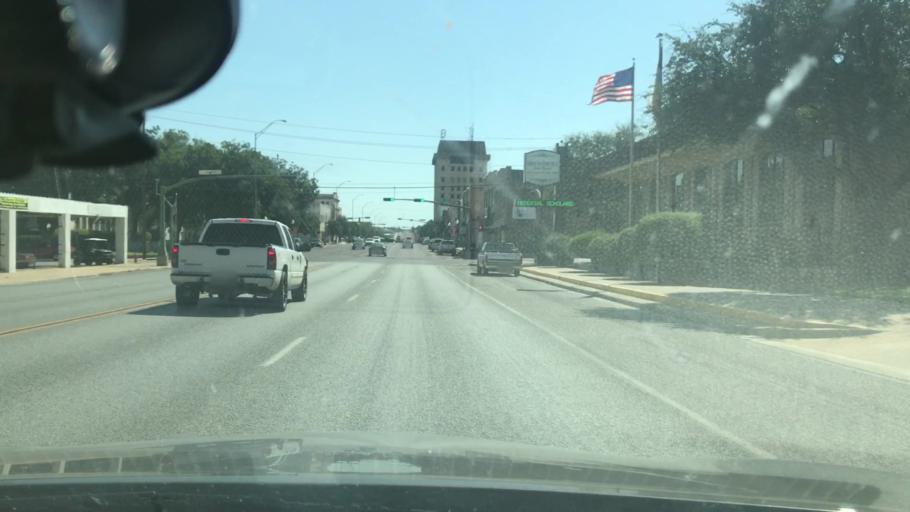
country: US
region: Texas
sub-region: Stephens County
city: Breckenridge
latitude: 32.7554
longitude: -98.9059
